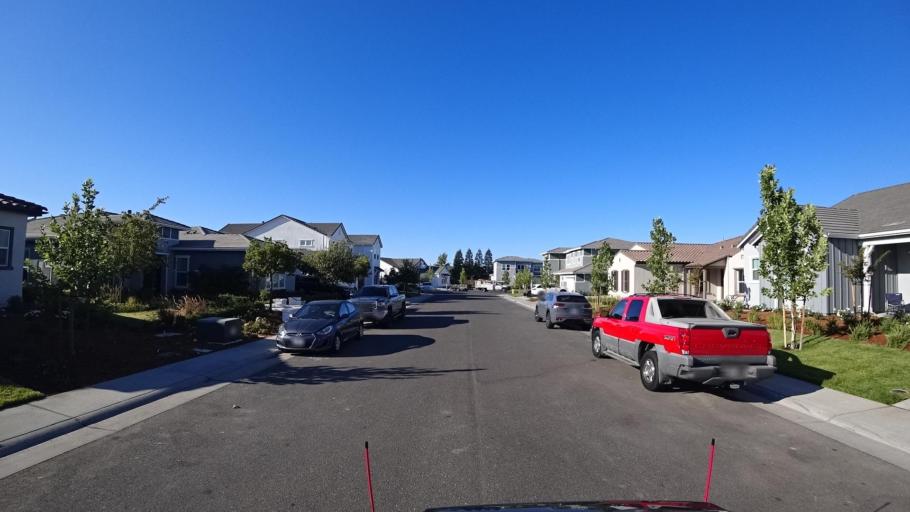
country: US
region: California
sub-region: Placer County
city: Rocklin
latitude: 38.8260
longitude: -121.2658
